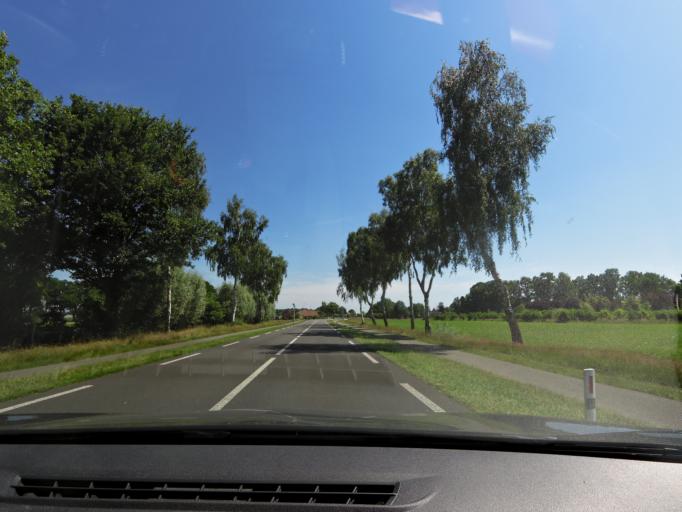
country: NL
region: Gelderland
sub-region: Berkelland
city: Neede
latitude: 52.1504
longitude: 6.6081
